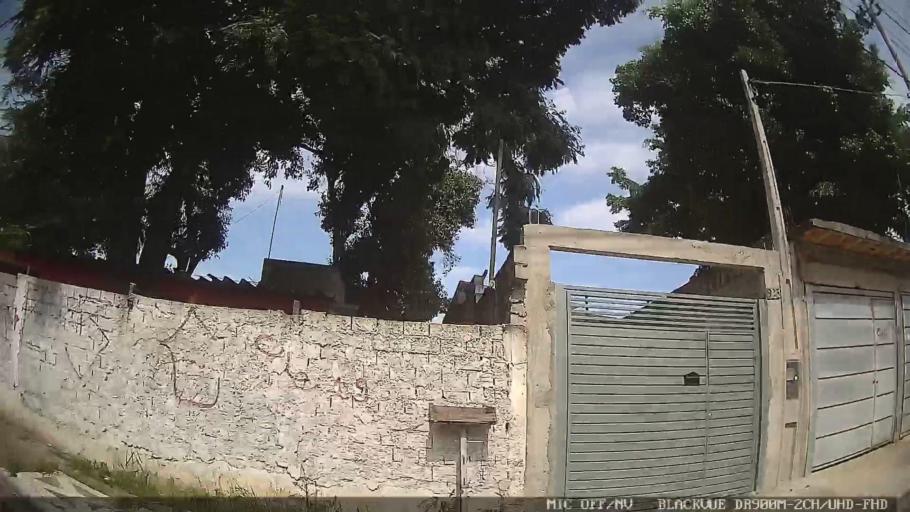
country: BR
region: Sao Paulo
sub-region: Suzano
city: Suzano
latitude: -23.5112
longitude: -46.3005
